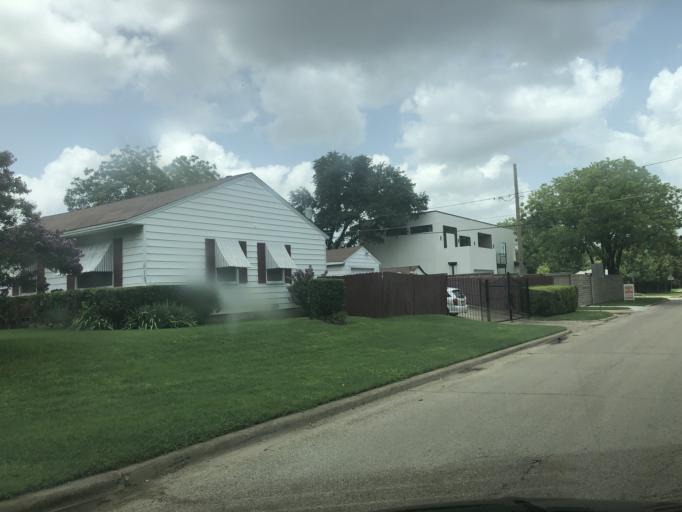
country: US
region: Texas
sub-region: Dallas County
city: University Park
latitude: 32.8689
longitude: -96.8488
